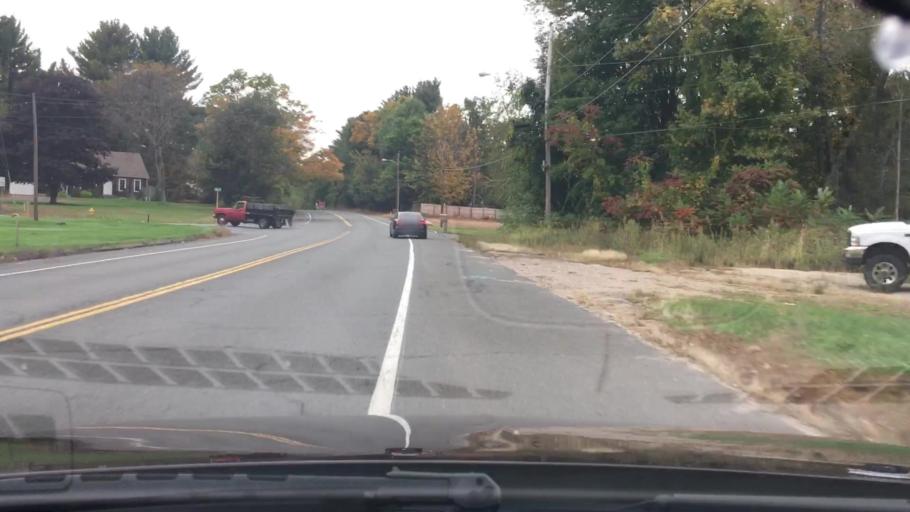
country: US
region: Massachusetts
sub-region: Hampden County
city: East Longmeadow
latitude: 42.0483
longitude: -72.4772
